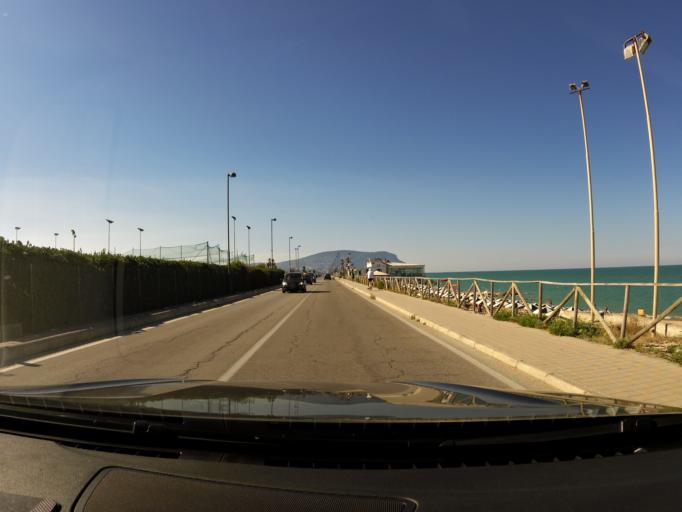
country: IT
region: The Marches
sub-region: Provincia di Macerata
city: Porto Recanati
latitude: 43.4549
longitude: 13.6522
